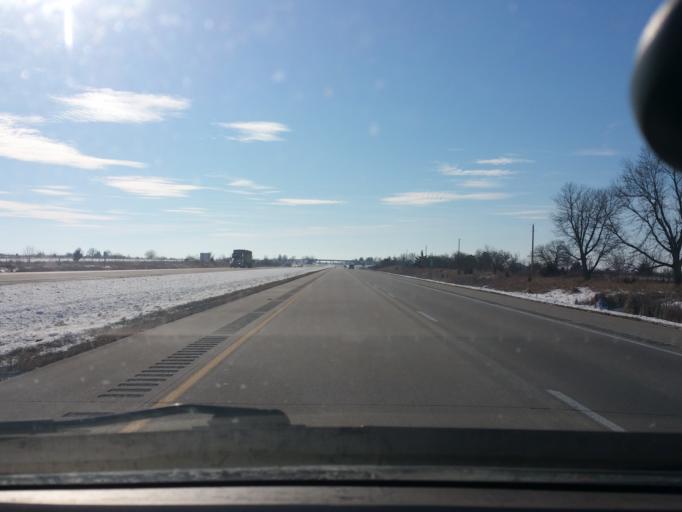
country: US
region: Iowa
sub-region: Clarke County
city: Osceola
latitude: 40.9822
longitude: -93.7977
